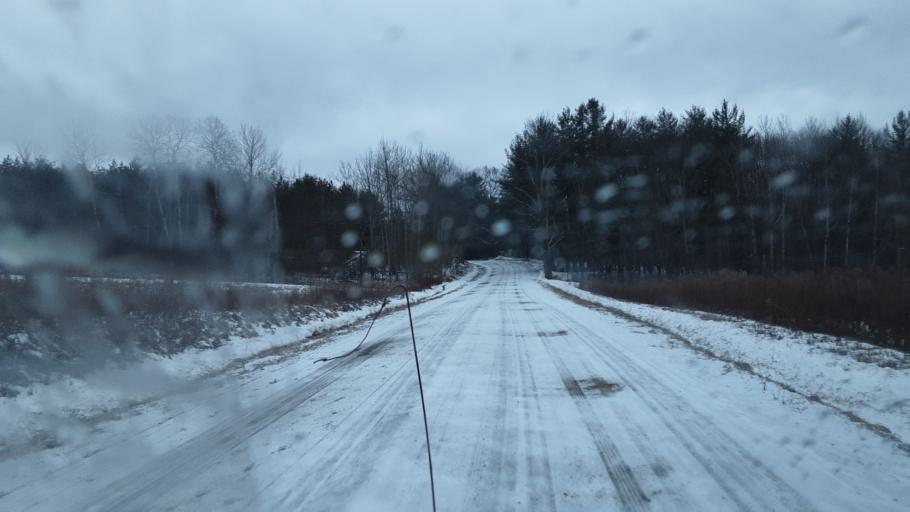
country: US
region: New York
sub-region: Allegany County
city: Friendship
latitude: 42.2882
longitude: -78.1624
